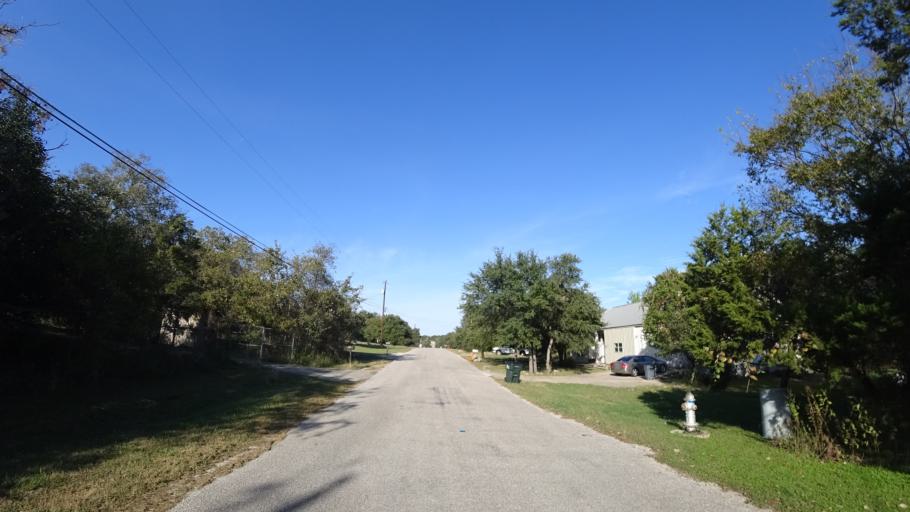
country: US
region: Texas
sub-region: Travis County
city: Barton Creek
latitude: 30.2431
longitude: -97.9152
